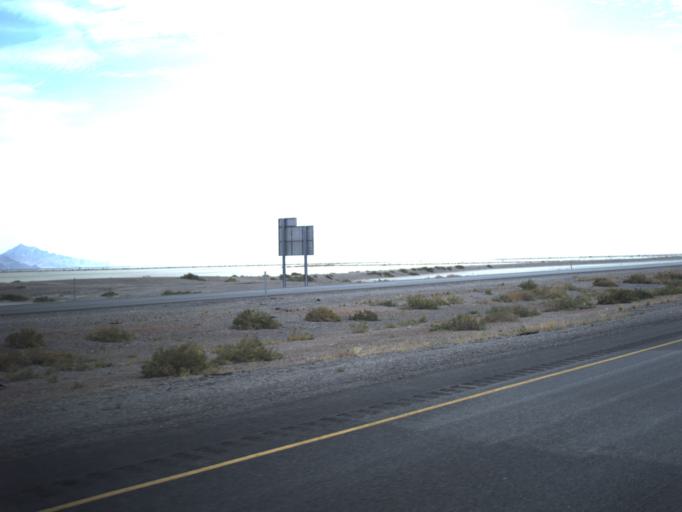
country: US
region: Utah
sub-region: Tooele County
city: Wendover
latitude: 40.7413
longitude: -113.9627
